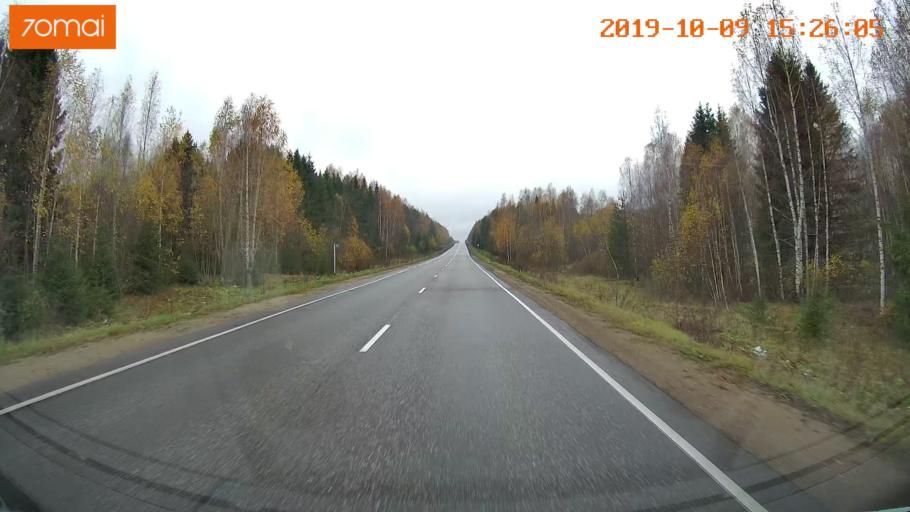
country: RU
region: Kostroma
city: Susanino
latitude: 58.0225
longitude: 41.4125
